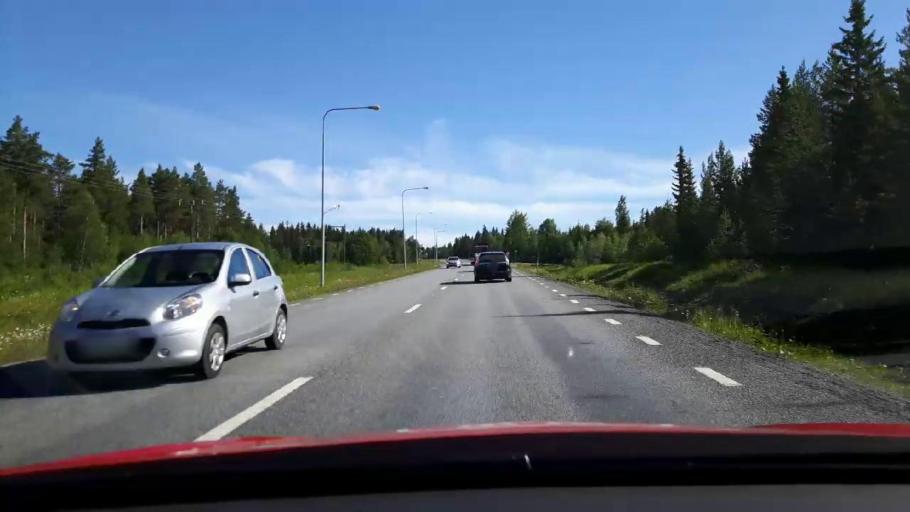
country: SE
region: Jaemtland
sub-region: OEstersunds Kommun
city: Lit
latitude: 63.3784
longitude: 14.8857
